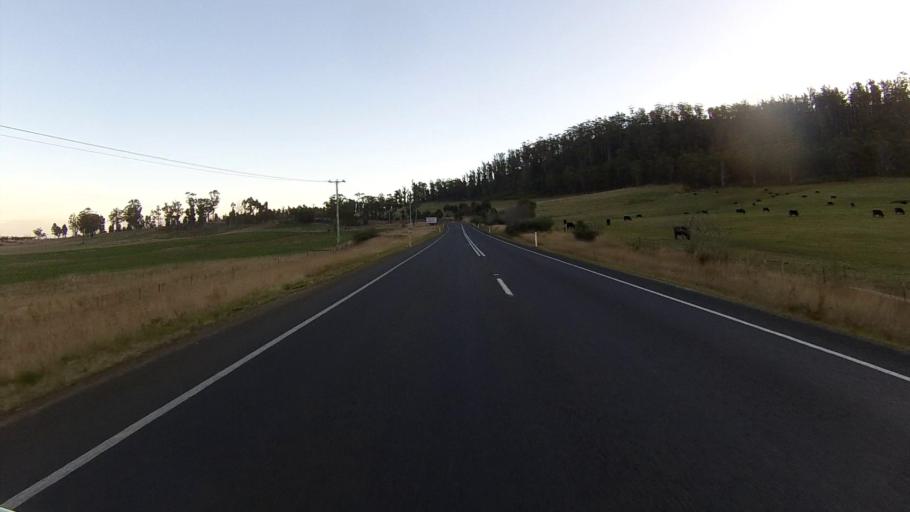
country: AU
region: Tasmania
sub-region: Sorell
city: Sorell
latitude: -42.8197
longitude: 147.7459
